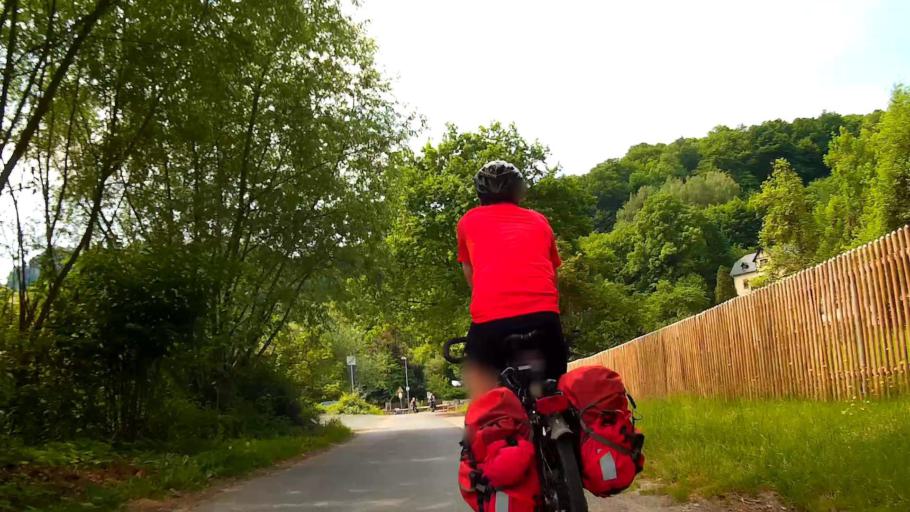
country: DE
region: Saxony
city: Konigstein
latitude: 50.9295
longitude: 14.0555
